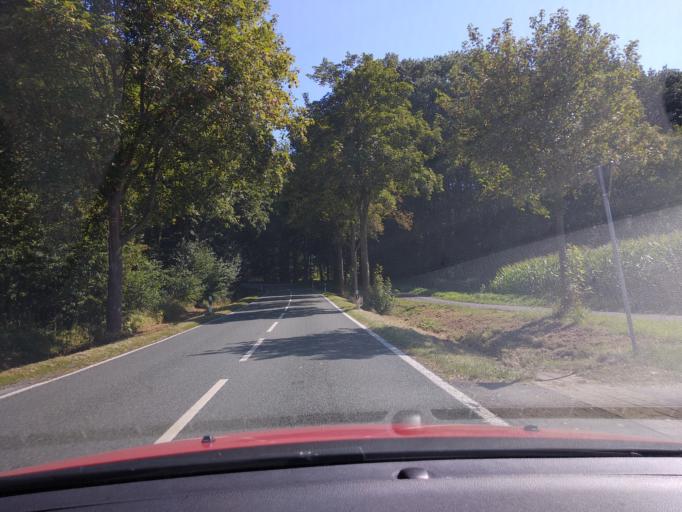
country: DE
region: North Rhine-Westphalia
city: Brakel
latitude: 51.6487
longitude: 9.1444
